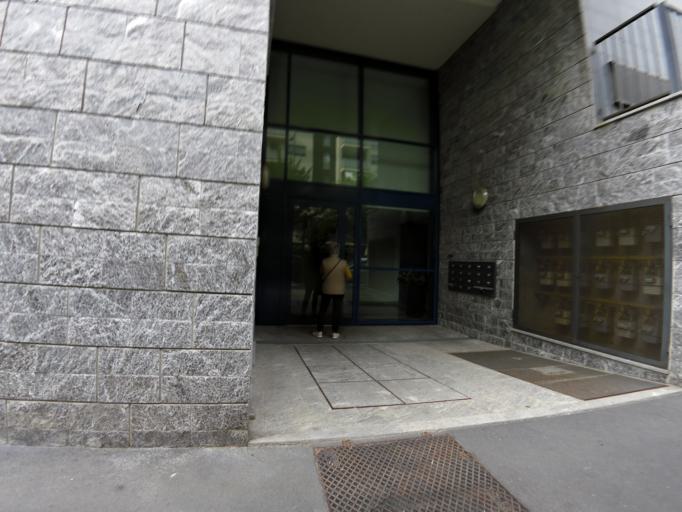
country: IT
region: Lombardy
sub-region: Citta metropolitana di Milano
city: Chiaravalle
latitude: 45.4358
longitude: 9.2443
